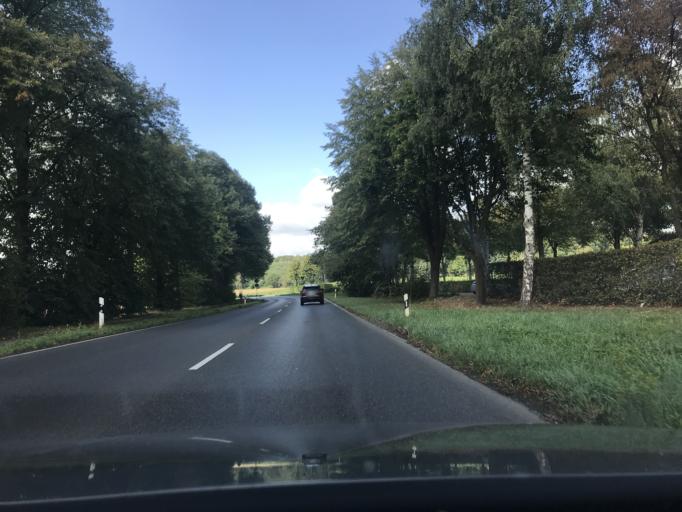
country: DE
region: North Rhine-Westphalia
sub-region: Regierungsbezirk Dusseldorf
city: Erkrath
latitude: 51.2266
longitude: 6.8873
